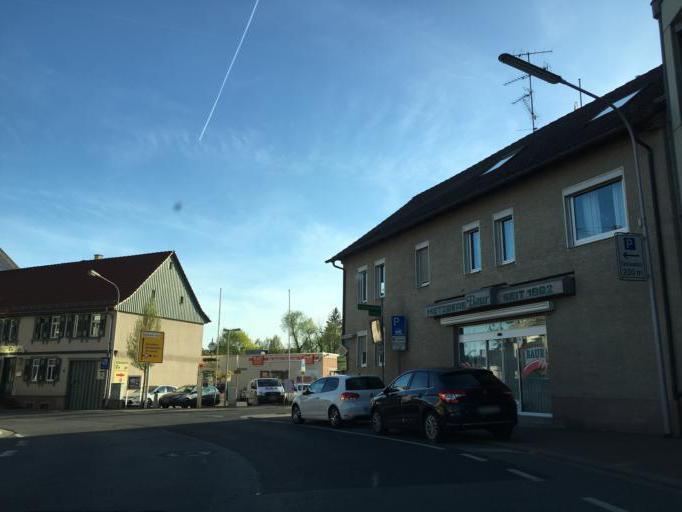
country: DE
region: Hesse
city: Reinheim
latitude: 49.8273
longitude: 8.8313
